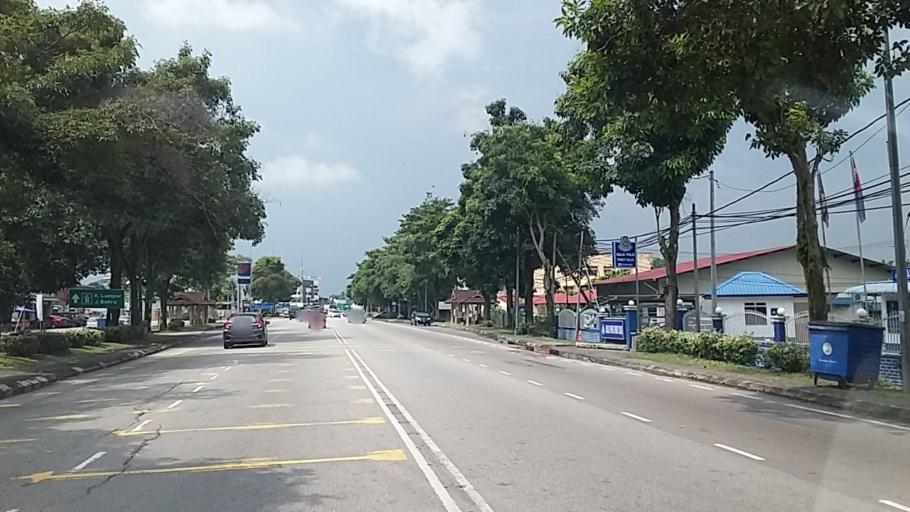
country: MY
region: Johor
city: Parit Raja
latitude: 1.8635
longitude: 103.1086
